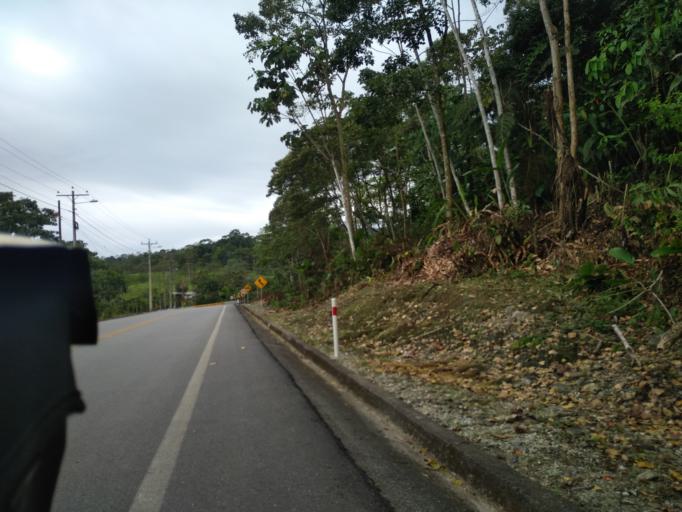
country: EC
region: Napo
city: Tena
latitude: -1.2460
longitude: -77.8784
